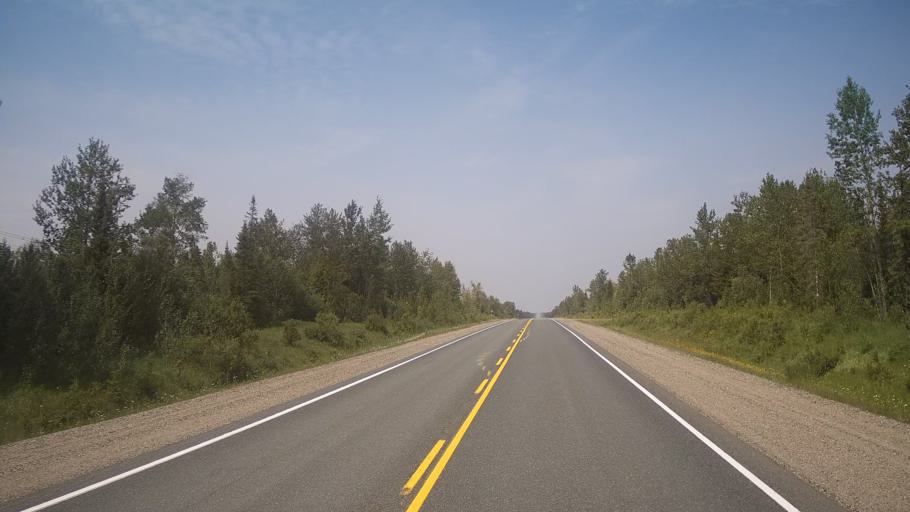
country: CA
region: Ontario
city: Timmins
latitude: 48.7742
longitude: -81.3633
